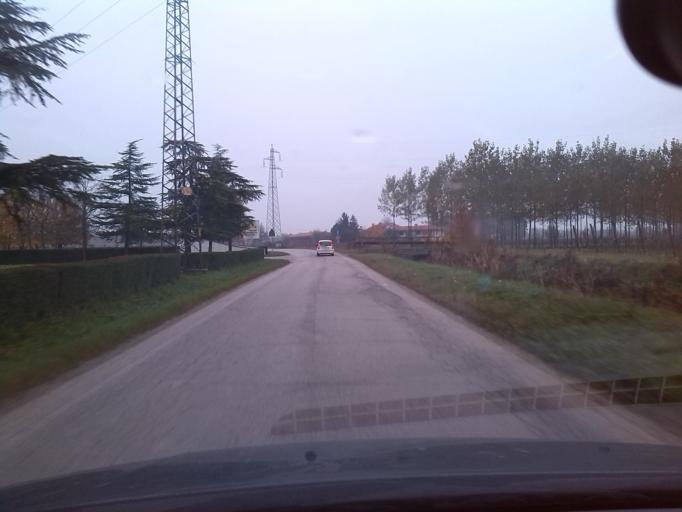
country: IT
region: Friuli Venezia Giulia
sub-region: Provincia di Gorizia
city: Moraro
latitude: 45.9357
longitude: 13.4782
